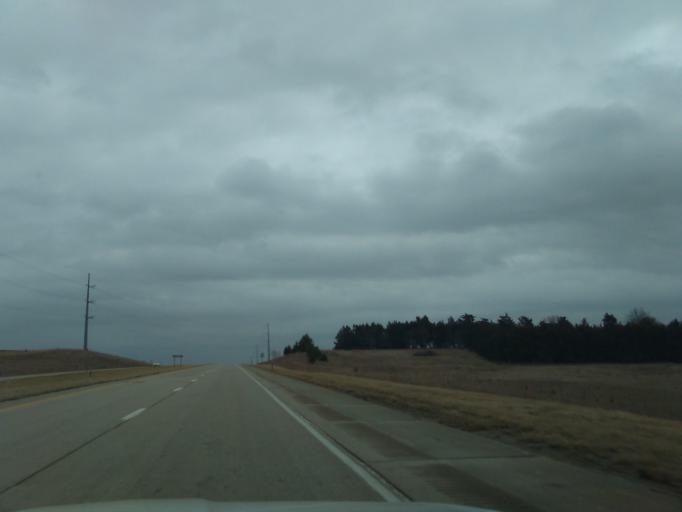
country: US
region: Nebraska
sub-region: Otoe County
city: Syracuse
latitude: 40.6697
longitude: -96.1065
